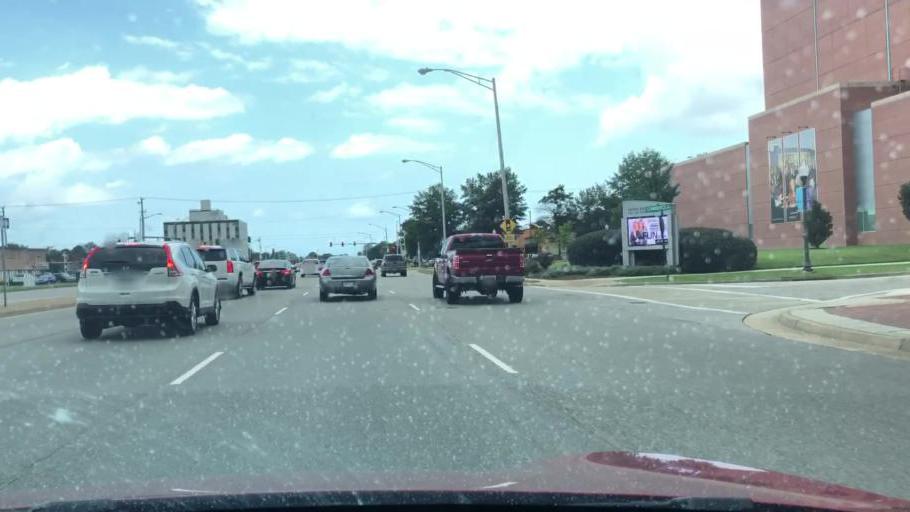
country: US
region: Virginia
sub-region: City of Chesapeake
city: Chesapeake
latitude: 36.8416
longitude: -76.1367
